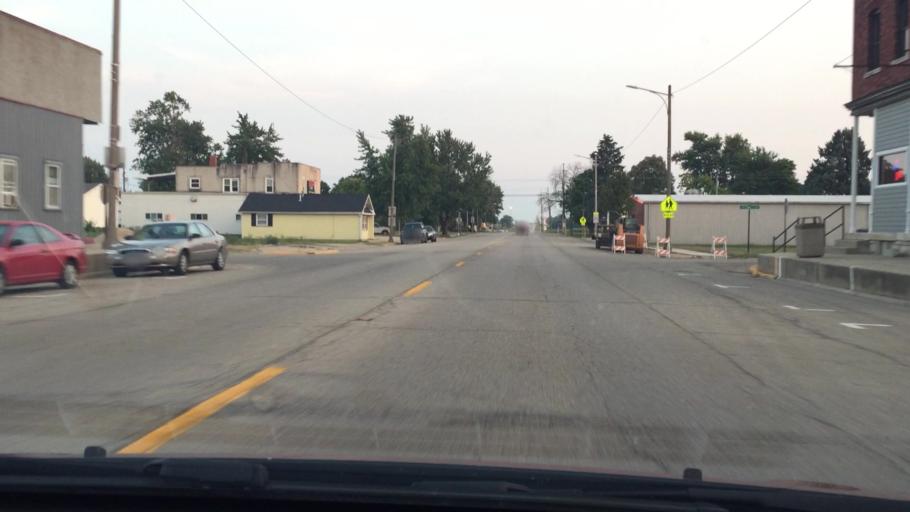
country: US
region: Illinois
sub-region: Bureau County
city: Ladd
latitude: 41.3809
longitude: -89.2191
